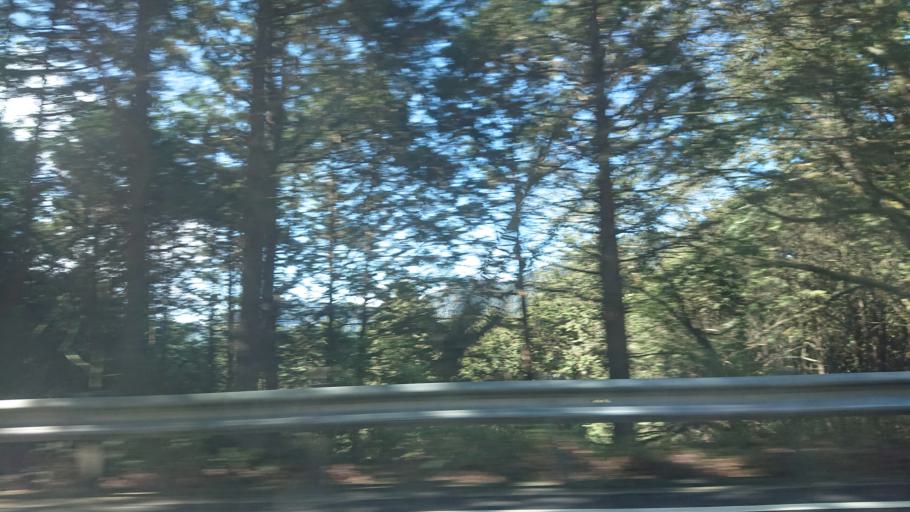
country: TW
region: Taiwan
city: Lugu
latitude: 23.4937
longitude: 120.8201
